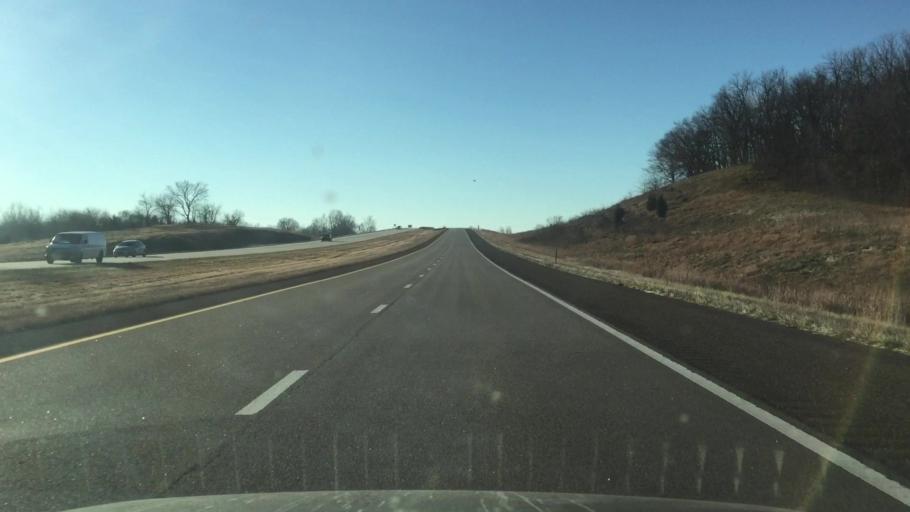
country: US
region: Kansas
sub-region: Miami County
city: Paola
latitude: 38.6404
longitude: -94.8359
